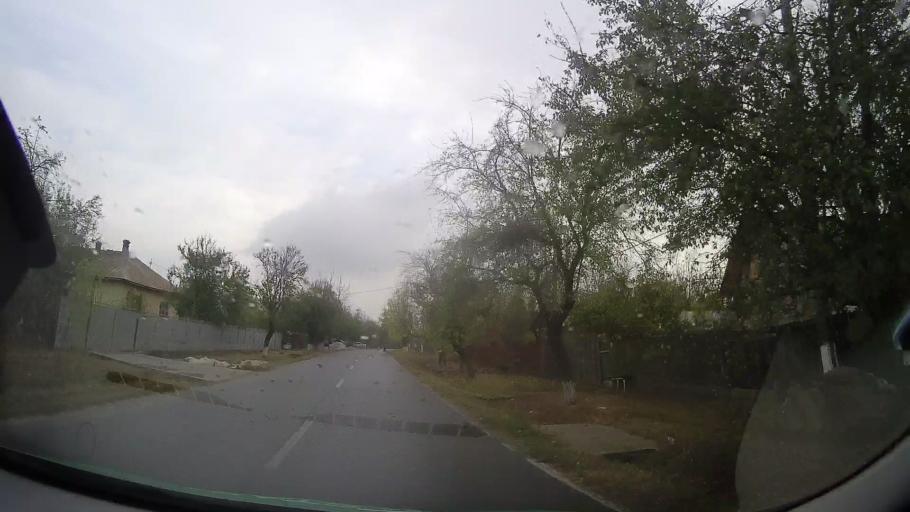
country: RO
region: Prahova
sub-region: Comuna Draganesti
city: Draganesti
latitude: 44.7908
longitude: 26.3114
